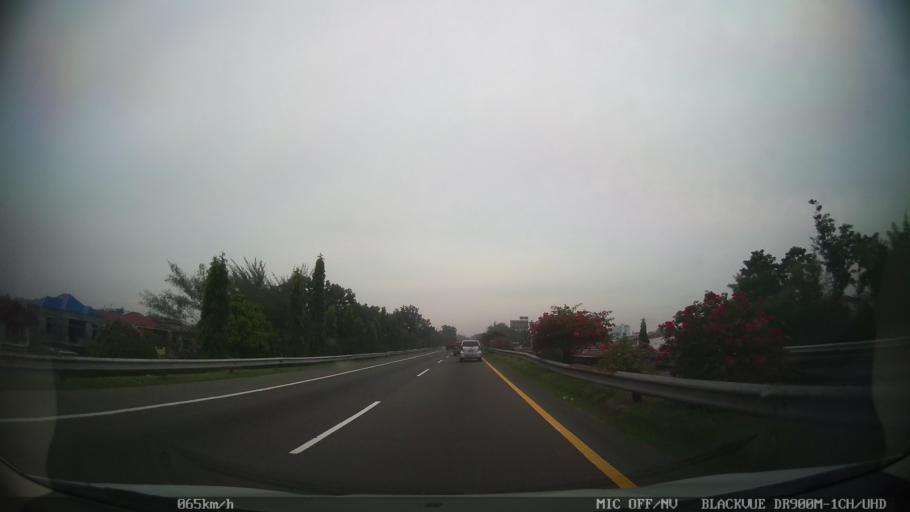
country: ID
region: North Sumatra
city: Medan
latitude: 3.5894
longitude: 98.7241
